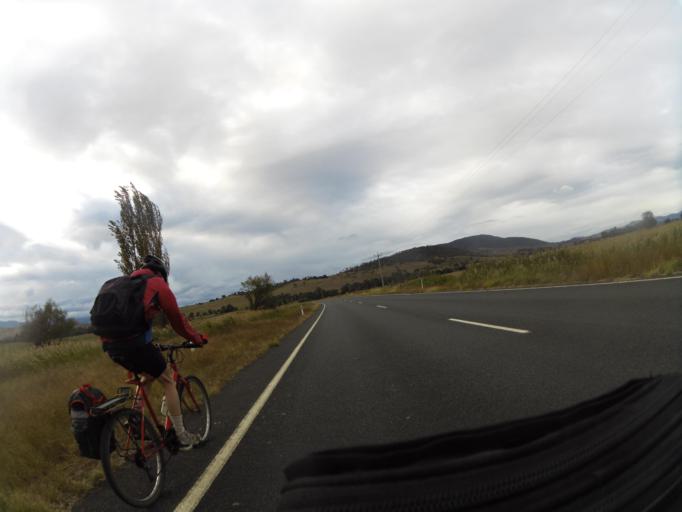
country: AU
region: New South Wales
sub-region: Snowy River
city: Jindabyne
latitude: -36.1189
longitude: 147.9810
